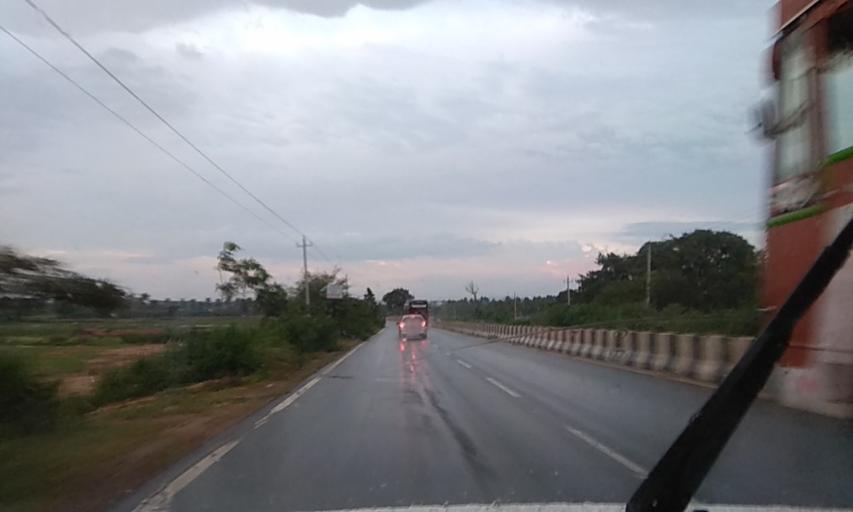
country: IN
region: Karnataka
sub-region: Mysore
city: Nanjangud
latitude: 12.0827
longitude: 76.6736
